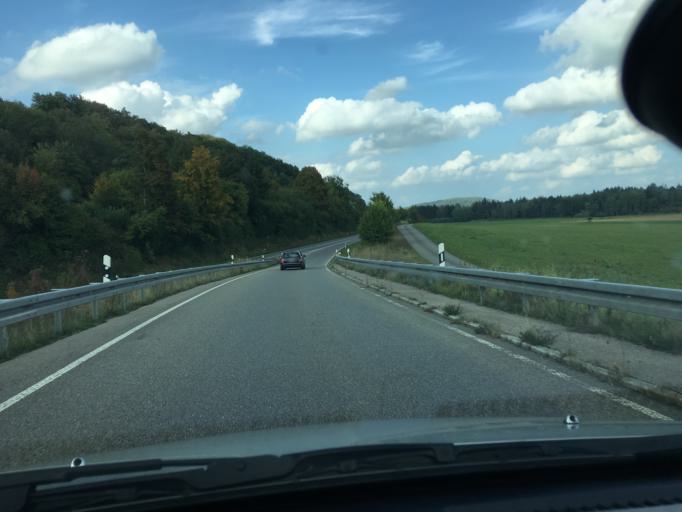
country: DE
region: Baden-Wuerttemberg
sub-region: Tuebingen Region
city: Hochdorf
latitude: 48.0501
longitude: 9.7970
